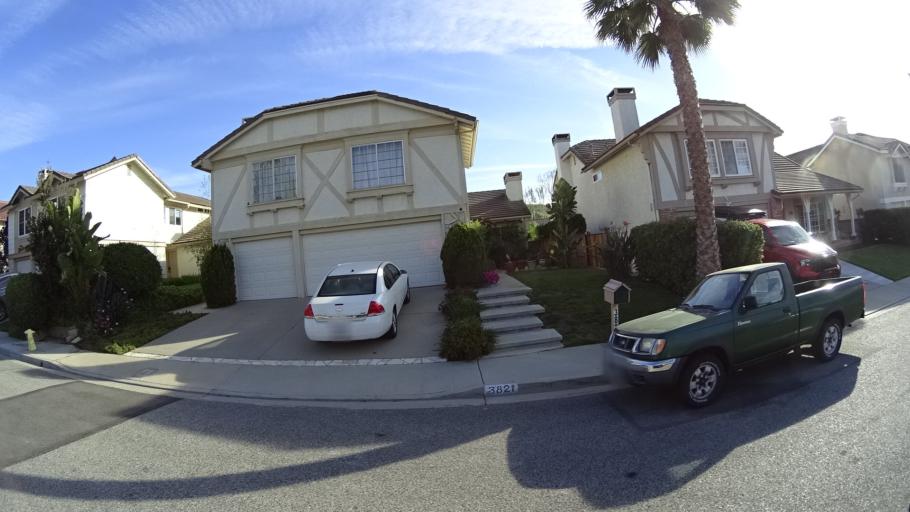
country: US
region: California
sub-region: Ventura County
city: Casa Conejo
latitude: 34.1880
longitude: -118.9568
